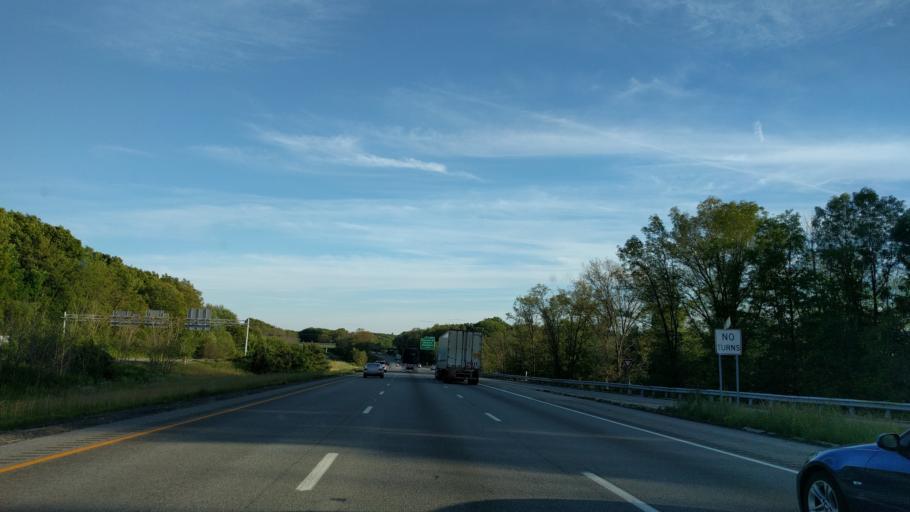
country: US
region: Massachusetts
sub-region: Middlesex County
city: Marlborough
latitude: 42.3390
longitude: -71.5757
